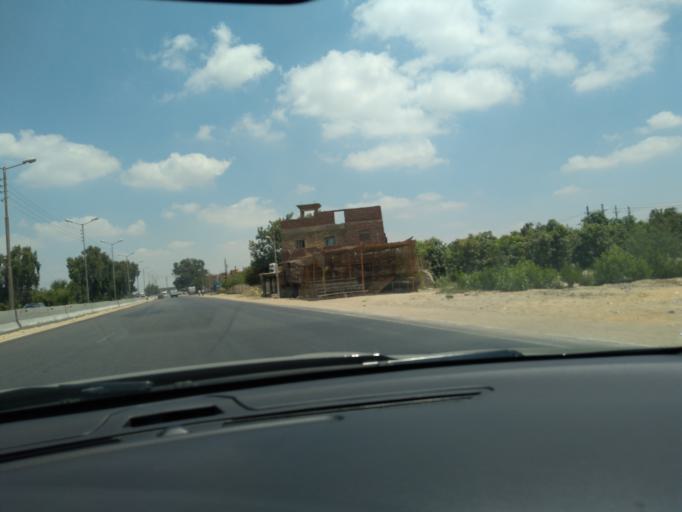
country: EG
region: Al Isma'iliyah
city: Ismailia
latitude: 30.6600
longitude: 32.2661
